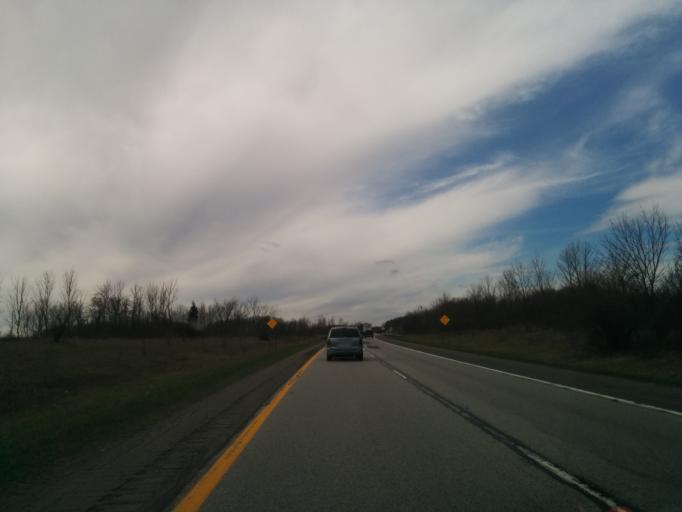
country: US
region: Michigan
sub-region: Ottawa County
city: Hudsonville
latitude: 42.8376
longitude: -85.8976
